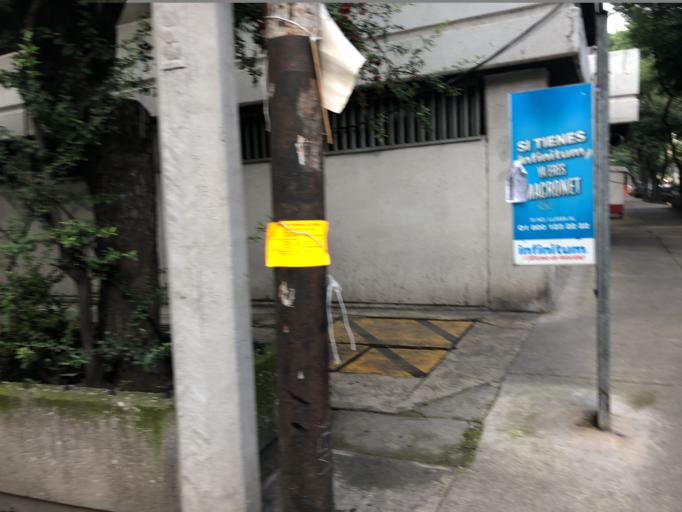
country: MX
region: Mexico City
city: Polanco
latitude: 19.4261
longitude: -99.1738
